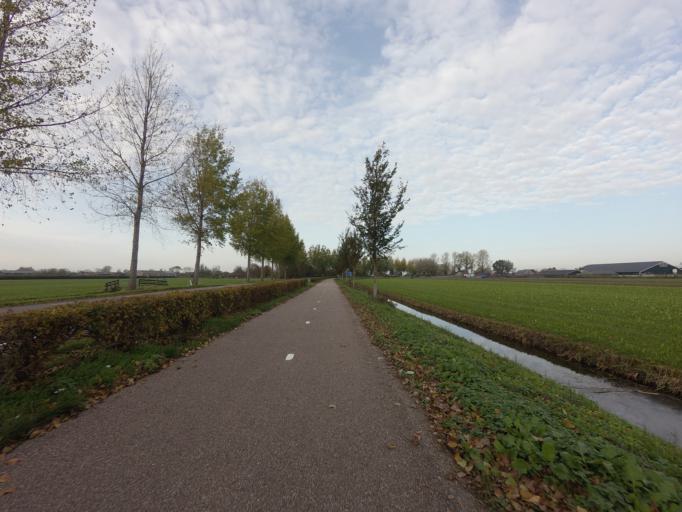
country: NL
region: Utrecht
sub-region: Gemeente IJsselstein
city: IJsselstein
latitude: 52.0057
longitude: 4.9996
